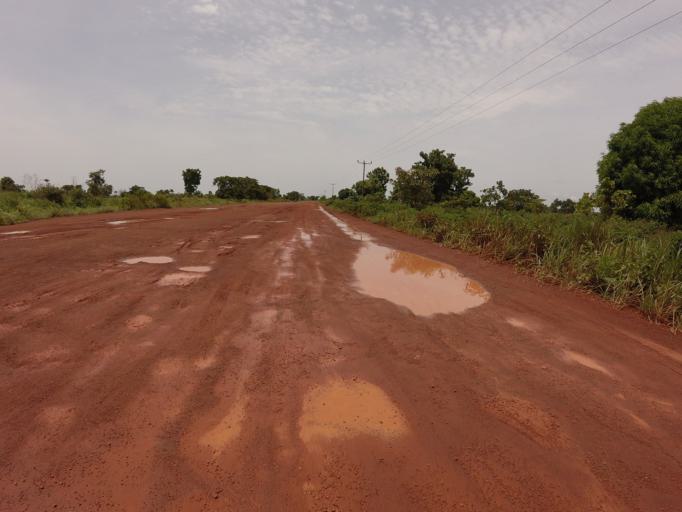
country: GH
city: Kpandae
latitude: 8.7545
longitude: 0.0686
